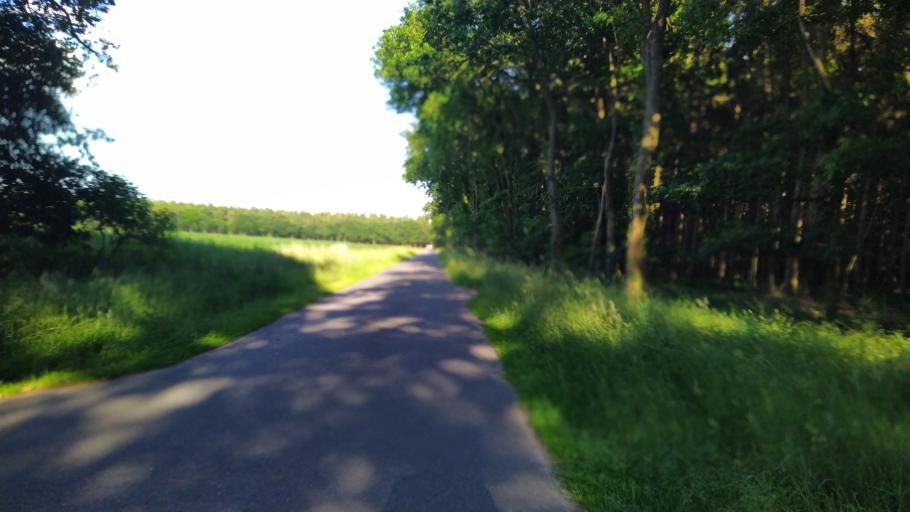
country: DE
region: Lower Saxony
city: Lintig
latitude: 53.5907
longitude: 8.9511
